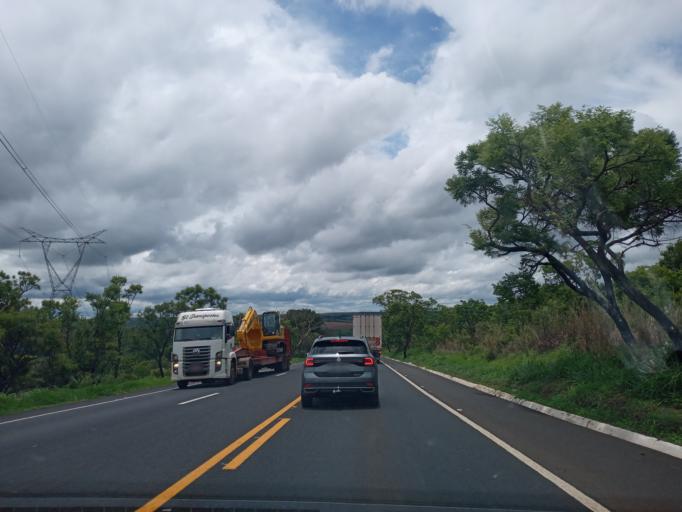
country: BR
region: Minas Gerais
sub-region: Uberaba
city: Uberaba
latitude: -19.2881
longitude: -47.6155
